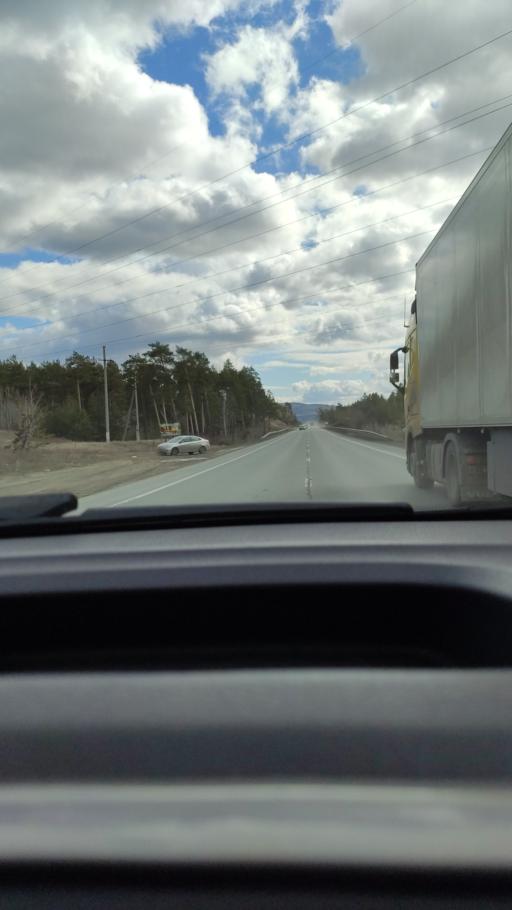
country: RU
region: Samara
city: Volzhskiy
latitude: 53.4492
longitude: 50.0956
